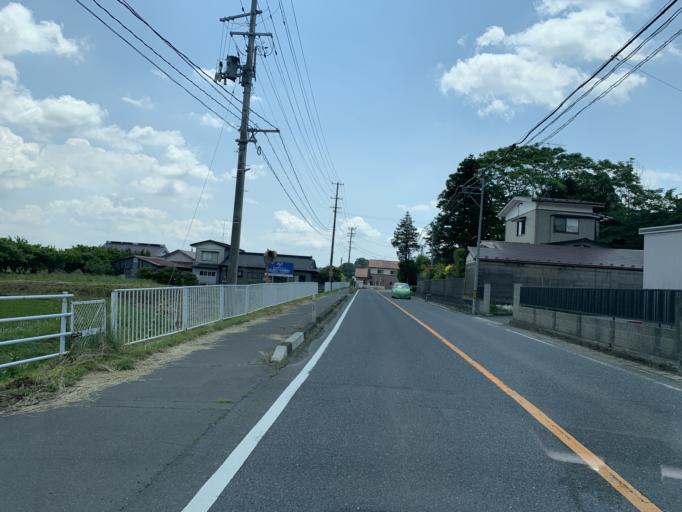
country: JP
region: Miyagi
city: Kogota
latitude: 38.5064
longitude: 141.0715
